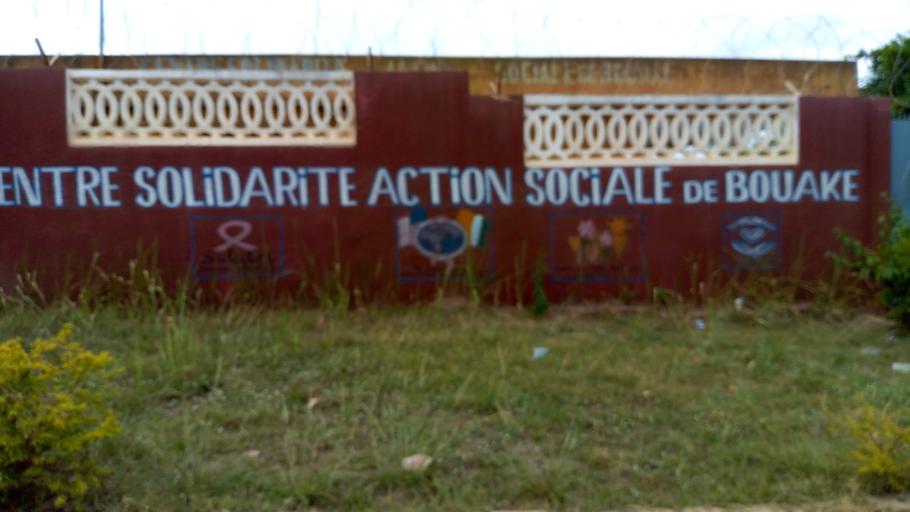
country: CI
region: Vallee du Bandama
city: Bouake
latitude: 7.6774
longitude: -5.0567
